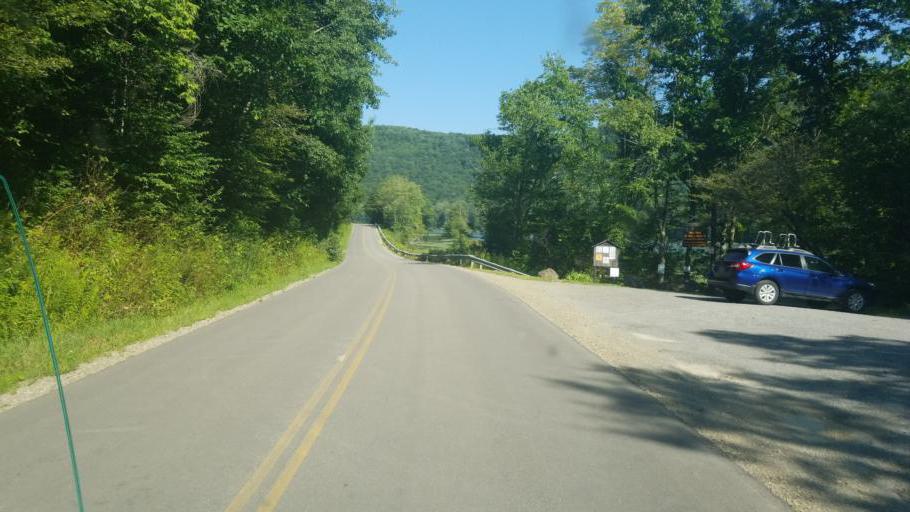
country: US
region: New York
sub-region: Allegany County
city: Wellsville
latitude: 42.0154
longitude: -77.9958
